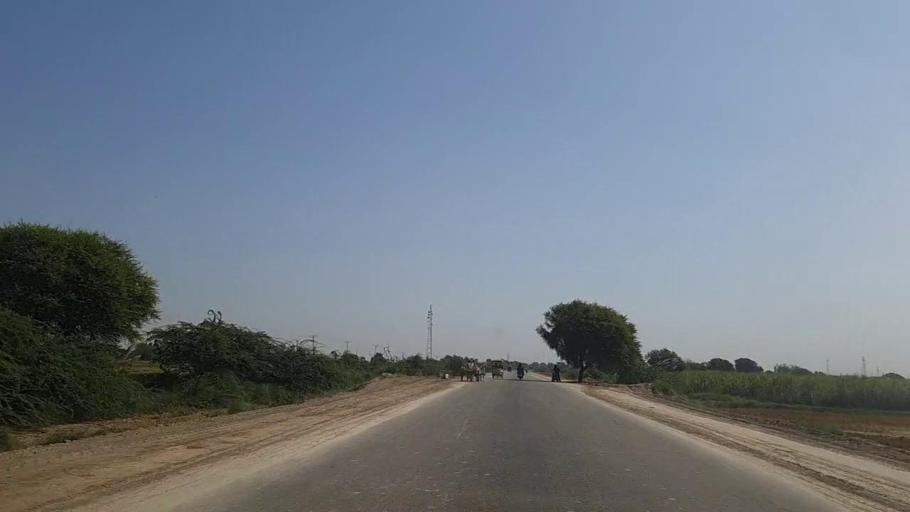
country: PK
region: Sindh
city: Mirpur Batoro
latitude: 24.7410
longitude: 68.2490
